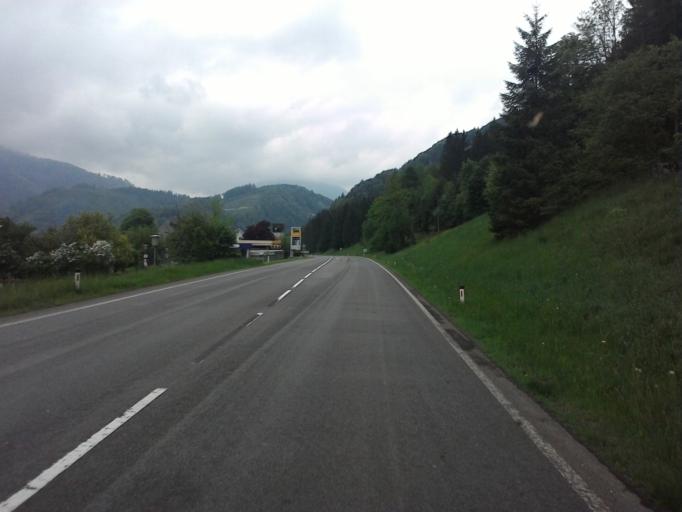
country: AT
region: Styria
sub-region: Politischer Bezirk Liezen
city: Altenmarkt bei Sankt Gallen
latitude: 47.7183
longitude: 14.6548
